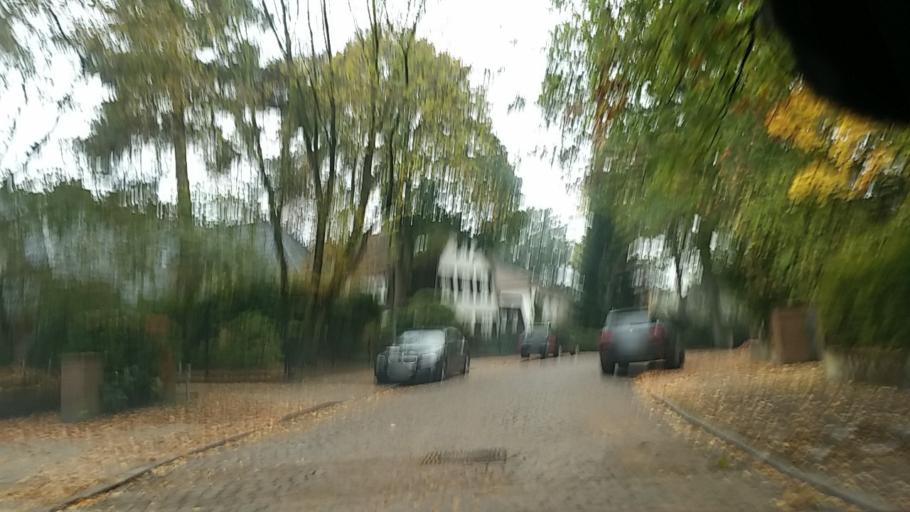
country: DE
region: Schleswig-Holstein
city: Rellingen
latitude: 53.5692
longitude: 9.7959
